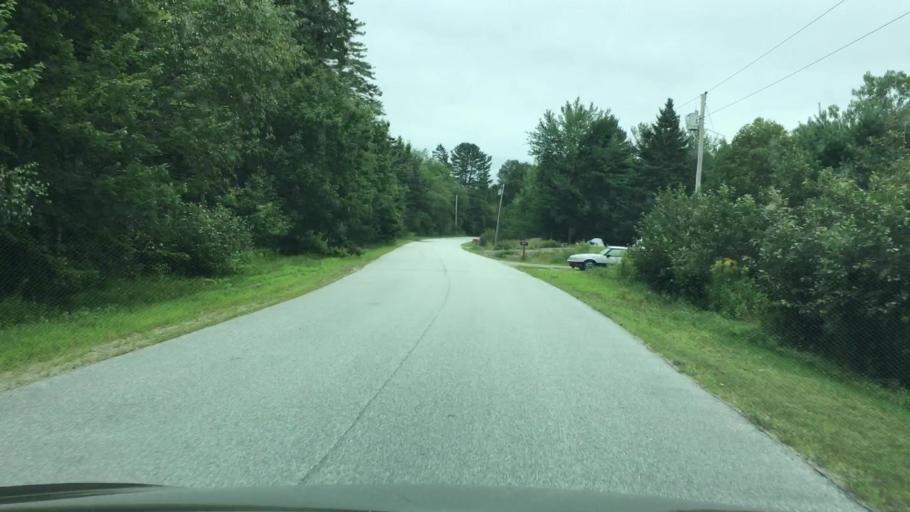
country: US
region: Maine
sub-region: Waldo County
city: Stockton Springs
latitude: 44.5259
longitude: -68.8240
